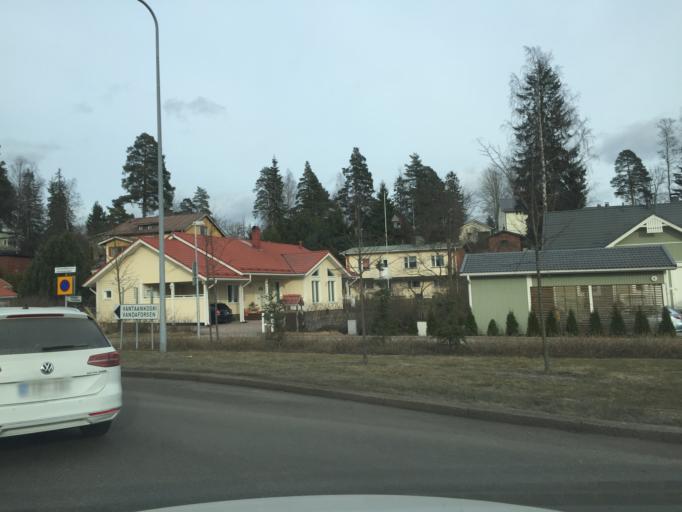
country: FI
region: Uusimaa
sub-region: Helsinki
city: Teekkarikylae
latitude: 60.2782
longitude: 24.8725
